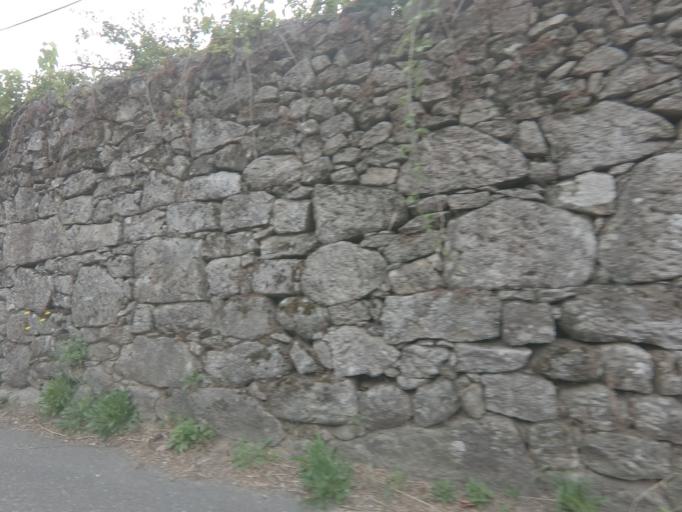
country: ES
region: Galicia
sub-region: Provincia de Pontevedra
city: Tui
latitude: 42.0458
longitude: -8.6563
